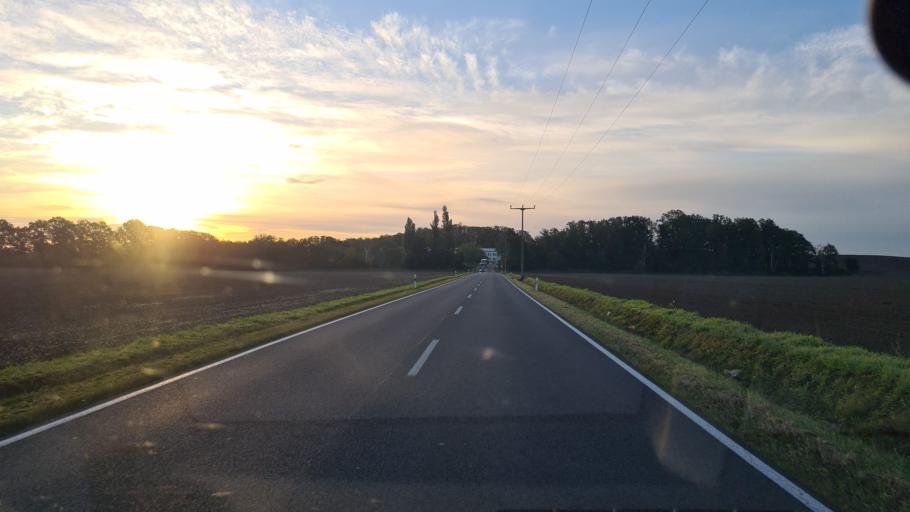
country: DE
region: Saxony
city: Eilenburg
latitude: 51.4352
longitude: 12.6196
